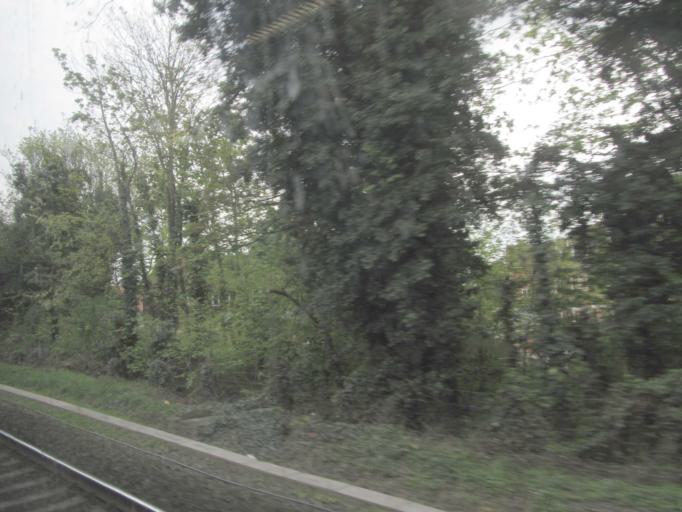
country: GB
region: England
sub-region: Slough
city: Slough
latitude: 51.5102
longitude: -0.5776
